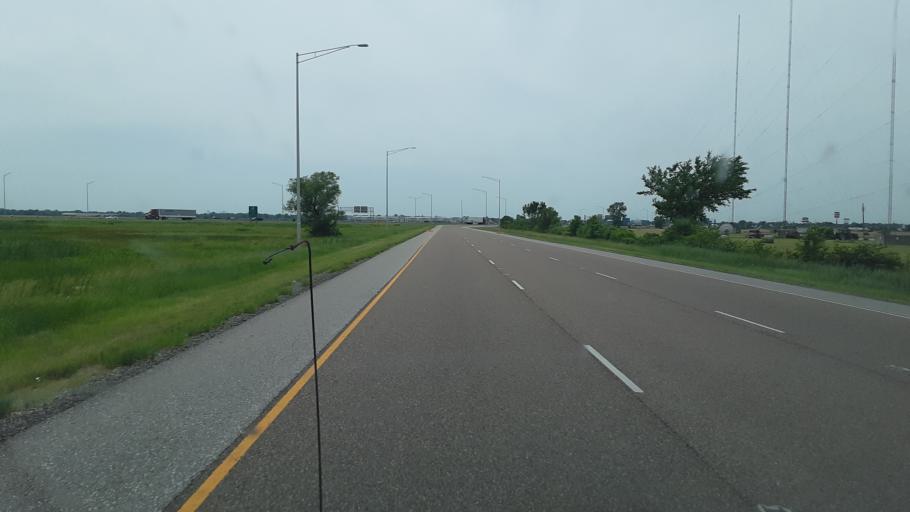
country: US
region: Illinois
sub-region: Madison County
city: Mitchell
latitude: 38.7593
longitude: -90.0478
